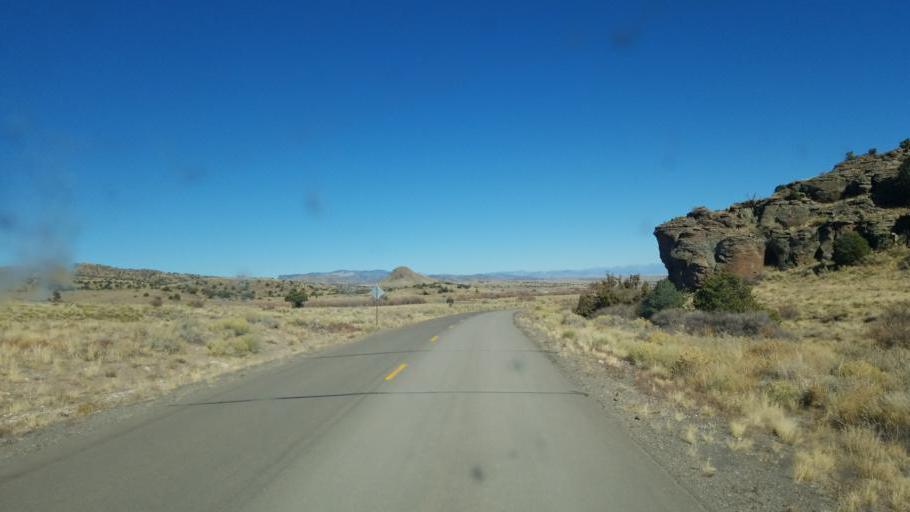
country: US
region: Colorado
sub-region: Rio Grande County
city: Del Norte
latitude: 37.6385
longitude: -106.3657
